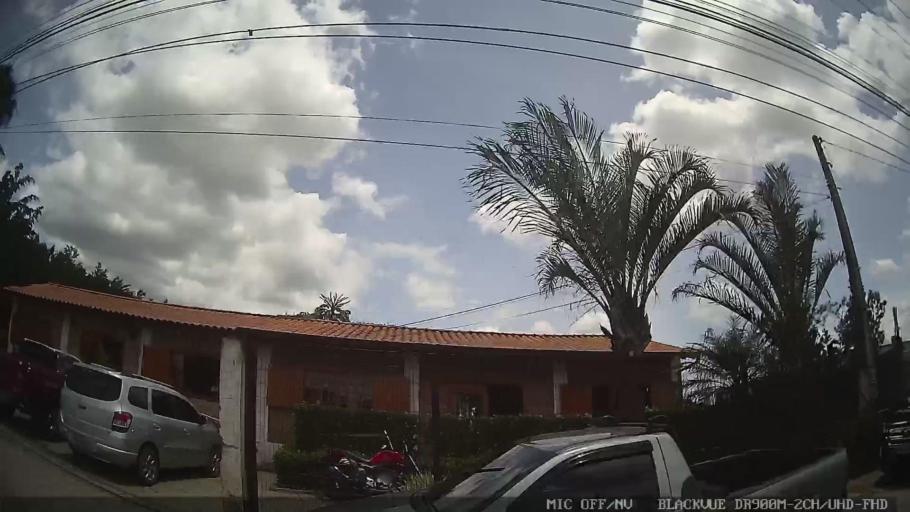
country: BR
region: Sao Paulo
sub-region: Suzano
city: Suzano
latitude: -23.5427
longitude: -46.2655
